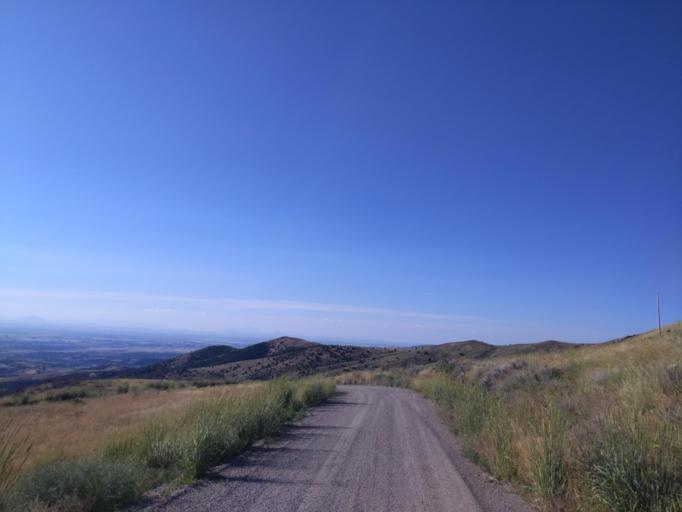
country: US
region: Idaho
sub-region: Bannock County
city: Pocatello
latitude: 42.8487
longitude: -112.3694
